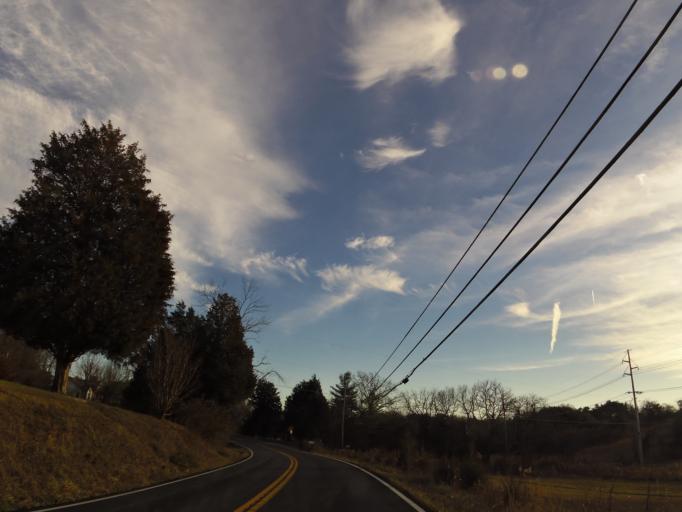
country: US
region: Tennessee
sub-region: Knox County
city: Mascot
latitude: 35.9854
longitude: -83.6957
